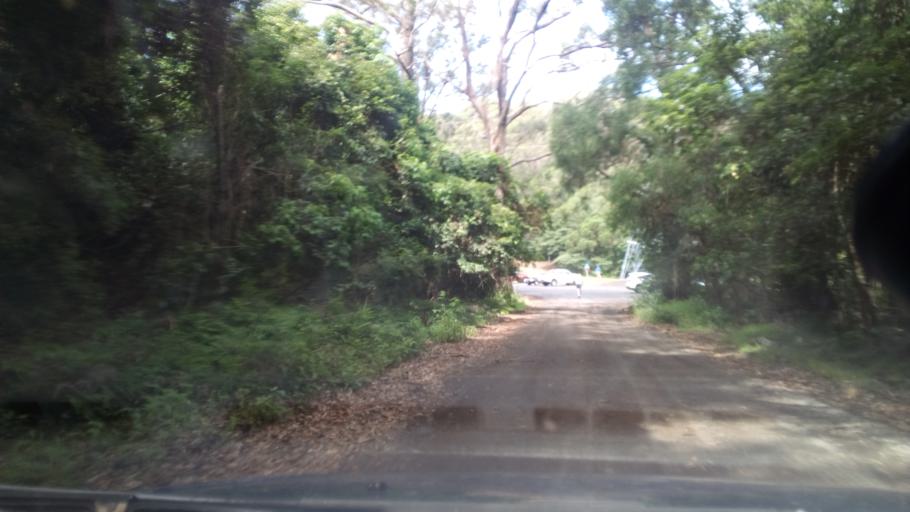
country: AU
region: New South Wales
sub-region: Wollongong
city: Cordeaux Heights
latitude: -34.4397
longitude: 150.7912
